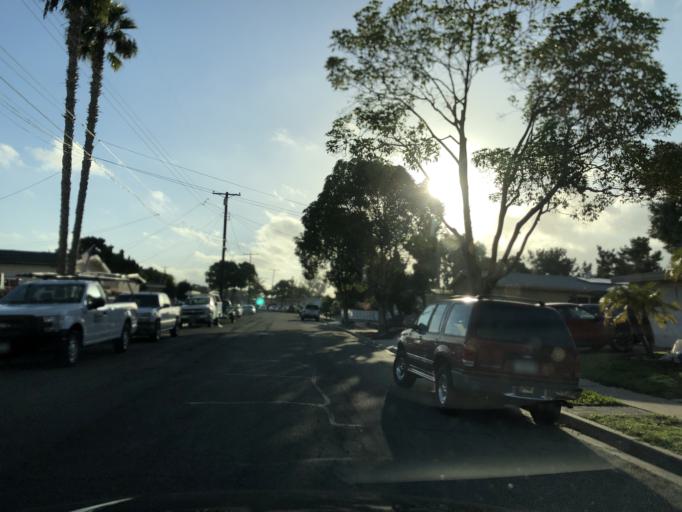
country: US
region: California
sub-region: San Diego County
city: San Diego
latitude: 32.8157
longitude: -117.1759
